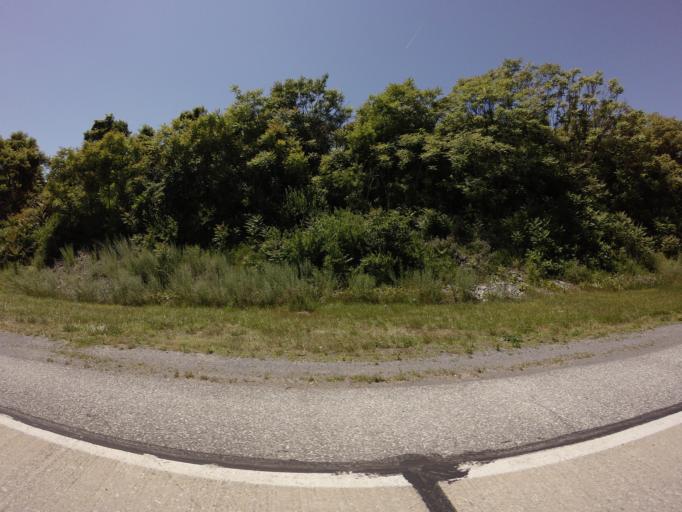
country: US
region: West Virginia
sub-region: Jefferson County
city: Ranson
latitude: 39.3010
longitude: -77.8407
